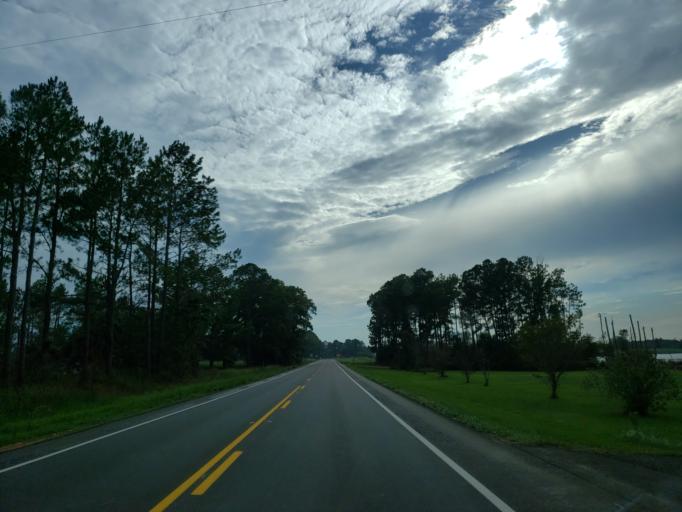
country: US
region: Georgia
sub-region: Irwin County
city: Ocilla
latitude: 31.5769
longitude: -83.2956
